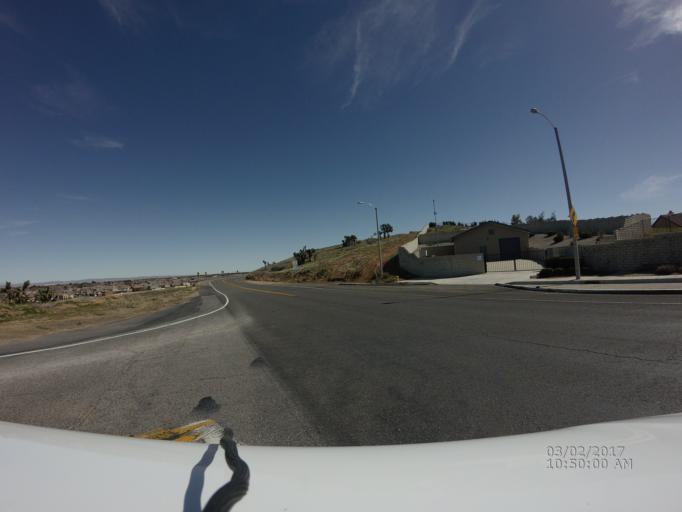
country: US
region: California
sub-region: Los Angeles County
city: Quartz Hill
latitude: 34.6456
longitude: -118.2076
